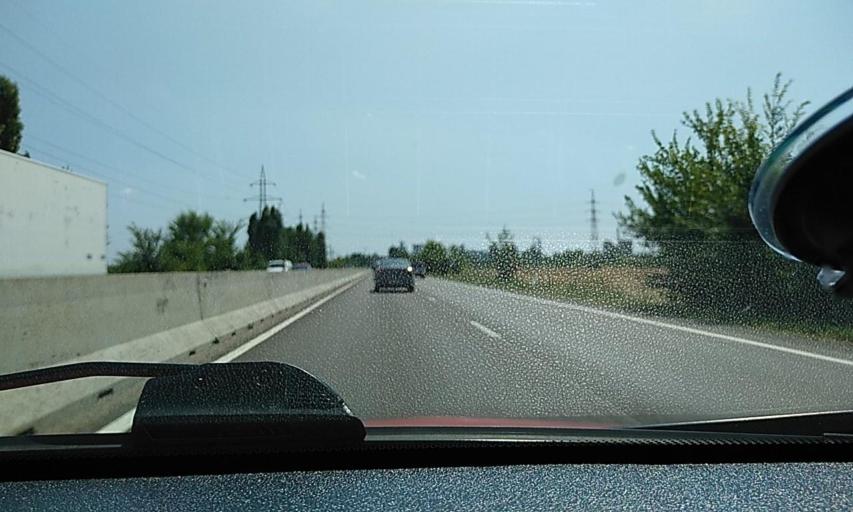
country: RO
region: Prahova
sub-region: Comuna Barcanesti
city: Tatarani
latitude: 44.8976
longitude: 26.0116
